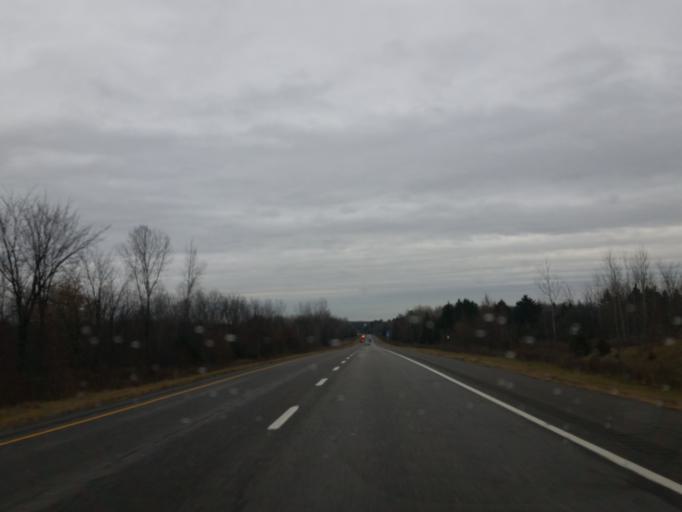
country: CA
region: Quebec
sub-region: Capitale-Nationale
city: Saint-Marc-des-Carrieres
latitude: 46.6324
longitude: -72.0141
